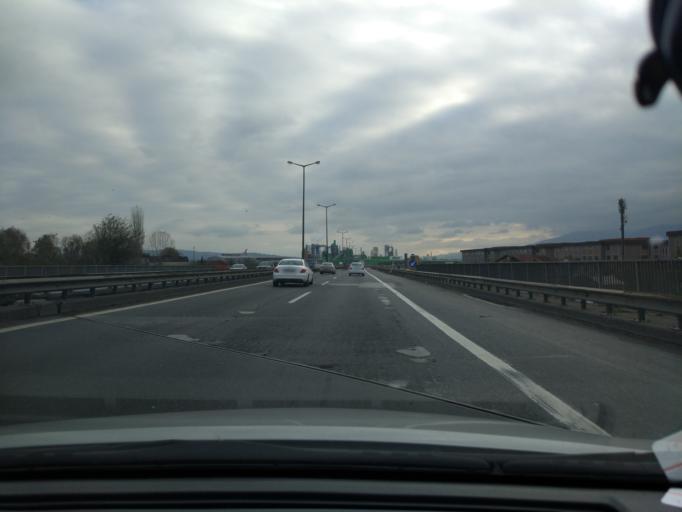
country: TR
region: Kocaeli
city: Kosekoy
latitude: 40.7662
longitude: 30.0218
